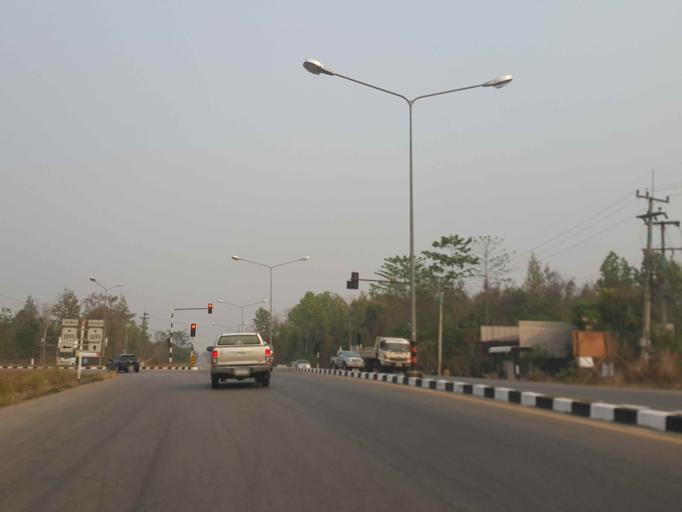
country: TH
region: Chiang Mai
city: Mae Taeng
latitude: 19.0872
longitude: 98.9047
